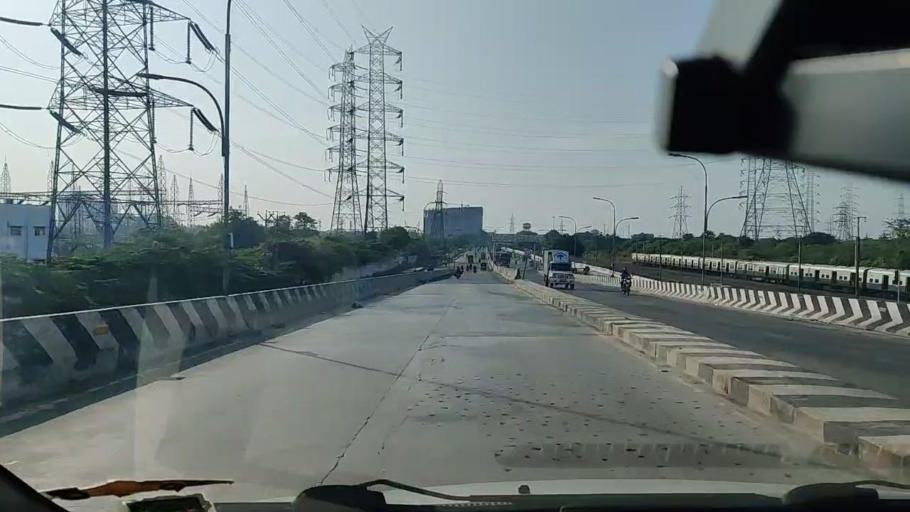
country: IN
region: Tamil Nadu
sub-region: Chennai
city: George Town
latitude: 13.1084
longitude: 80.2680
